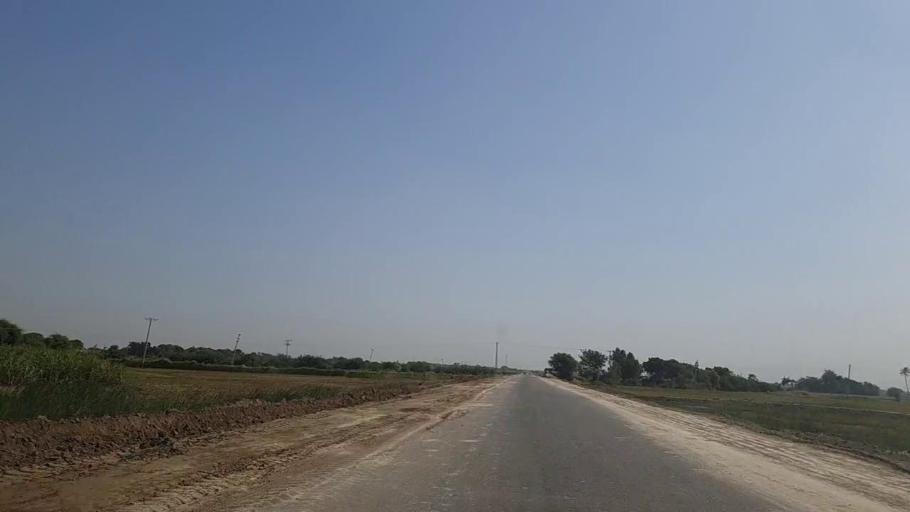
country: PK
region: Sindh
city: Mirpur Batoro
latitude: 24.7511
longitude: 68.2347
